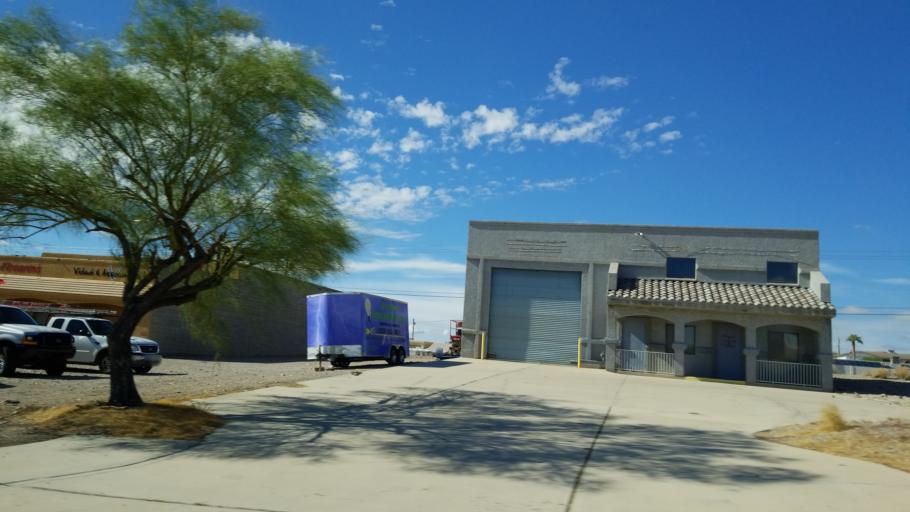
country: US
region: Arizona
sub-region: Mohave County
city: Lake Havasu City
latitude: 34.4973
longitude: -114.2873
